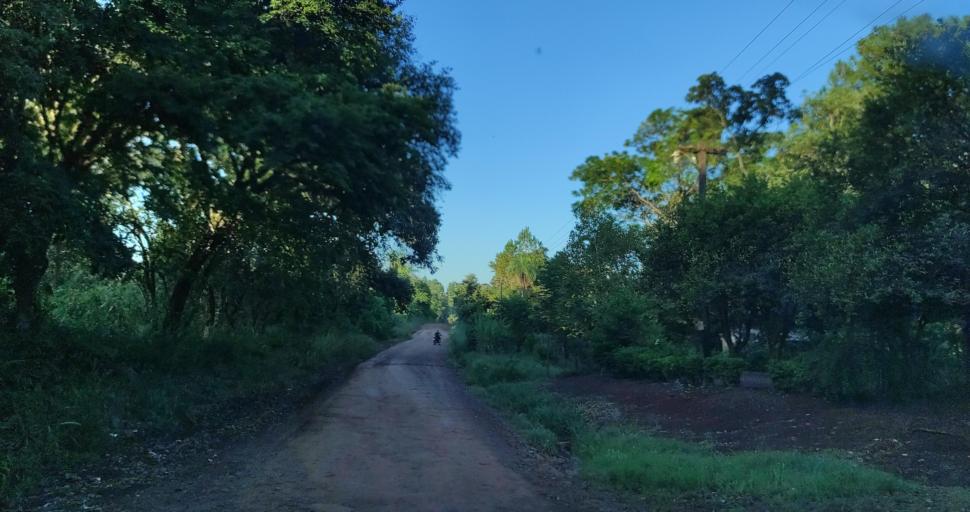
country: AR
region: Misiones
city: Gobernador Roca
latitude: -27.2221
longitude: -55.4288
